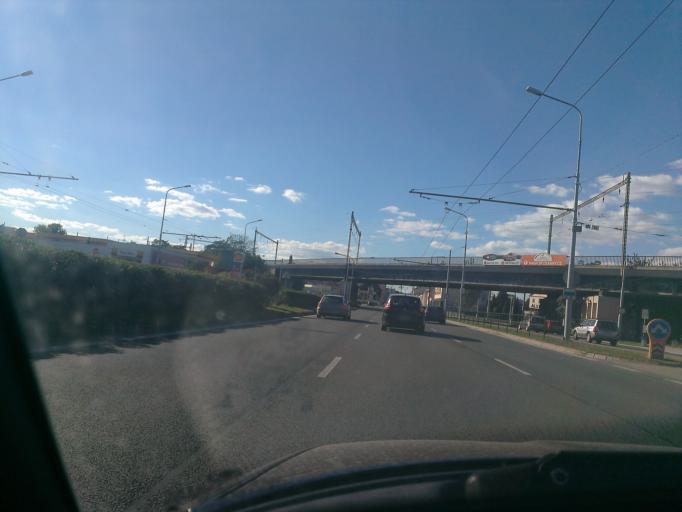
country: CZ
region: South Moravian
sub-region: Mesto Brno
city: Brno
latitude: 49.1898
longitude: 16.6356
